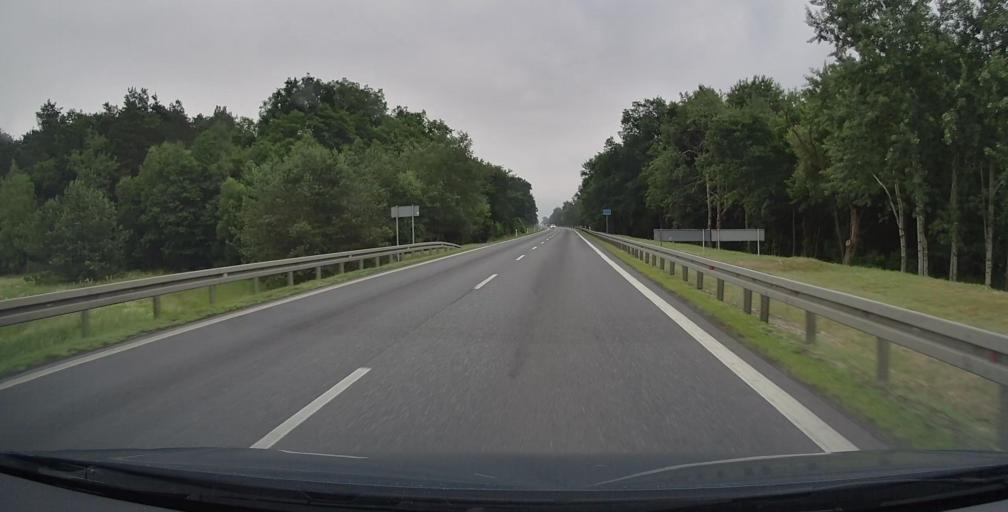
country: PL
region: Lublin Voivodeship
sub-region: Powiat bialski
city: Zalesie
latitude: 52.0343
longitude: 23.2871
